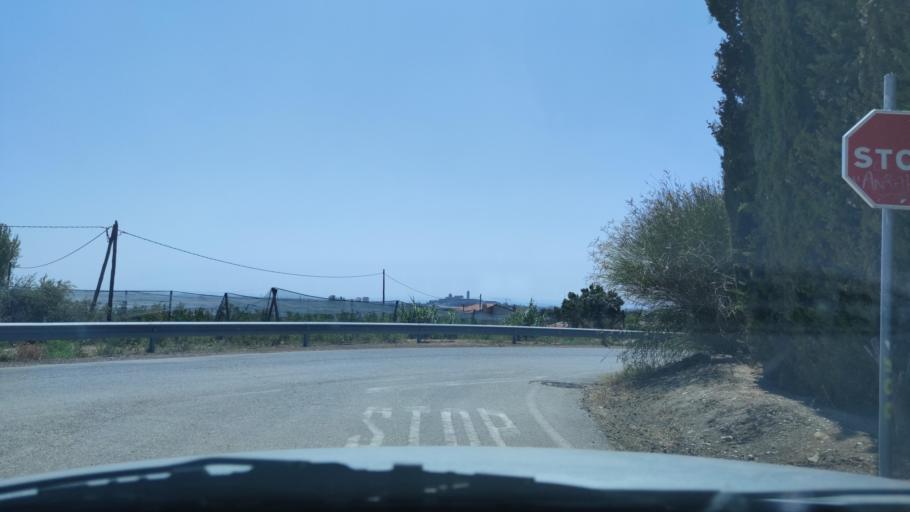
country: ES
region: Catalonia
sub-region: Provincia de Lleida
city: Lleida
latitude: 41.6375
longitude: 0.5976
